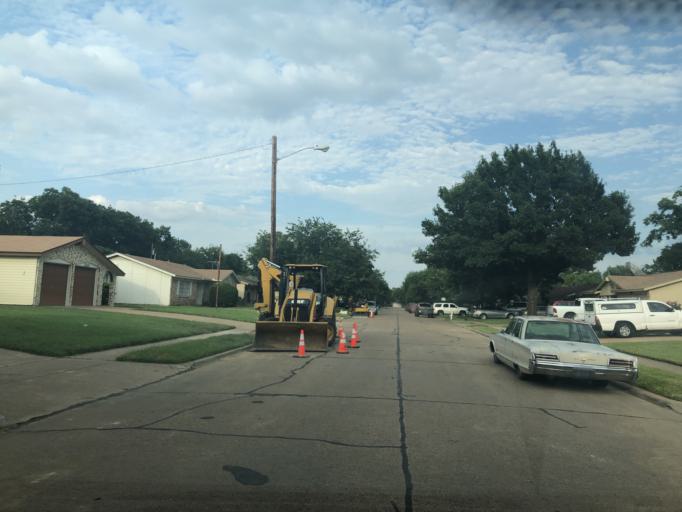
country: US
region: Texas
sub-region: Dallas County
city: Irving
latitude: 32.7875
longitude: -96.9723
